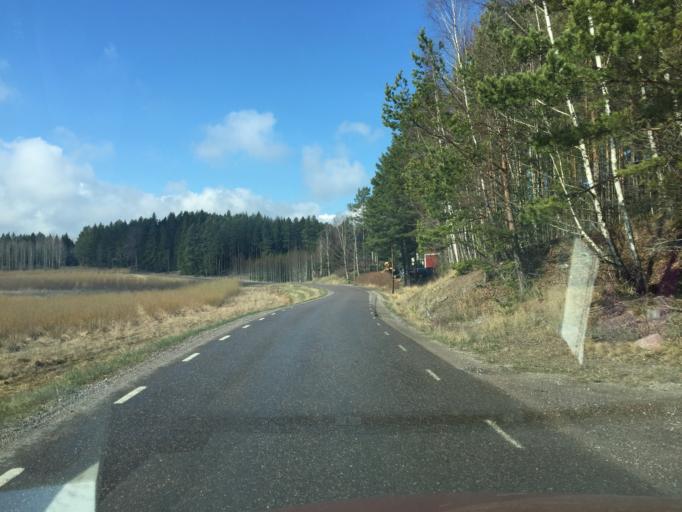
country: SE
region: Soedermanland
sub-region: Gnesta Kommun
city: Gnesta
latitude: 59.0393
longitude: 17.2463
